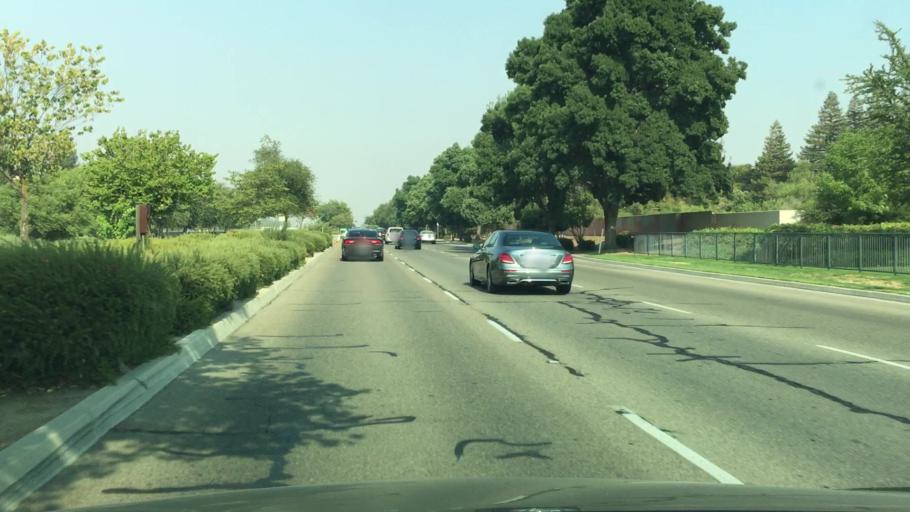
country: US
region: California
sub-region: Fresno County
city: West Park
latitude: 36.8370
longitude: -119.8769
